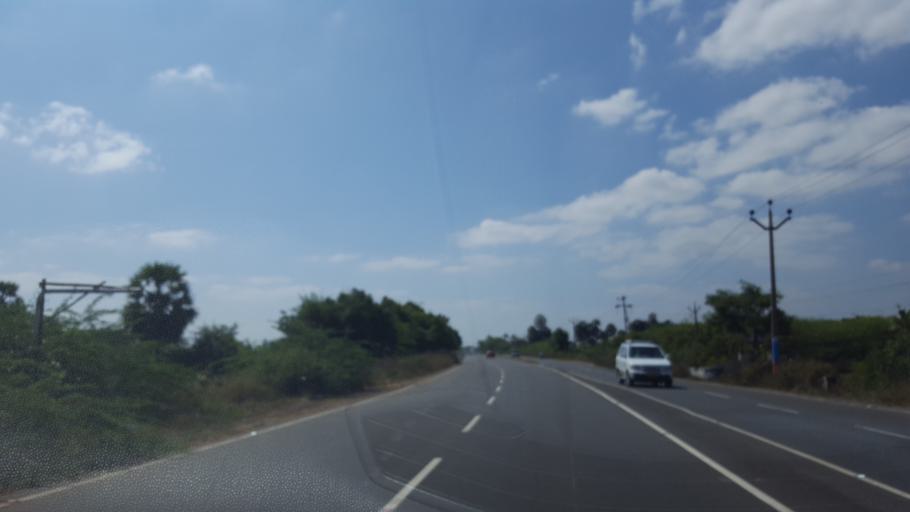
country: IN
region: Tamil Nadu
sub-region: Kancheepuram
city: Mamallapuram
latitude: 12.6393
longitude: 80.1720
